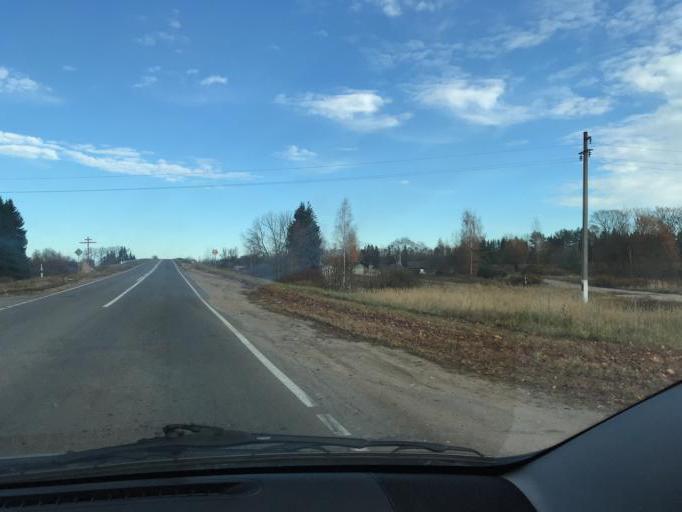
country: BY
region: Vitebsk
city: Haradok
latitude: 55.4962
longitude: 29.9669
